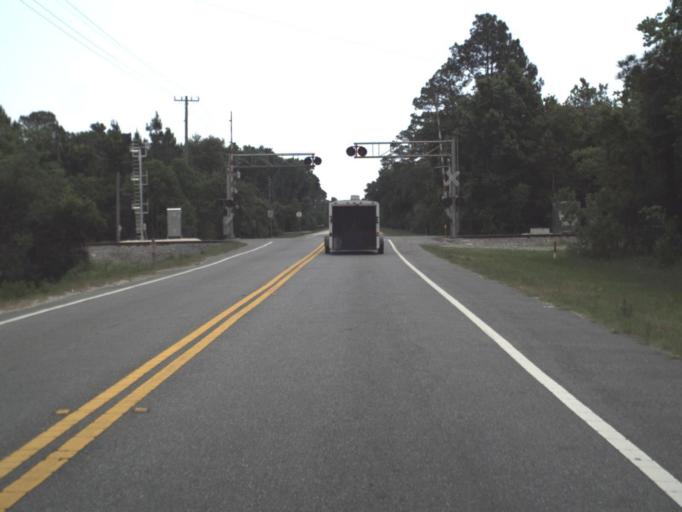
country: US
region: Florida
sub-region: Saint Johns County
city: Saint Augustine Shores
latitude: 29.7563
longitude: -81.3214
